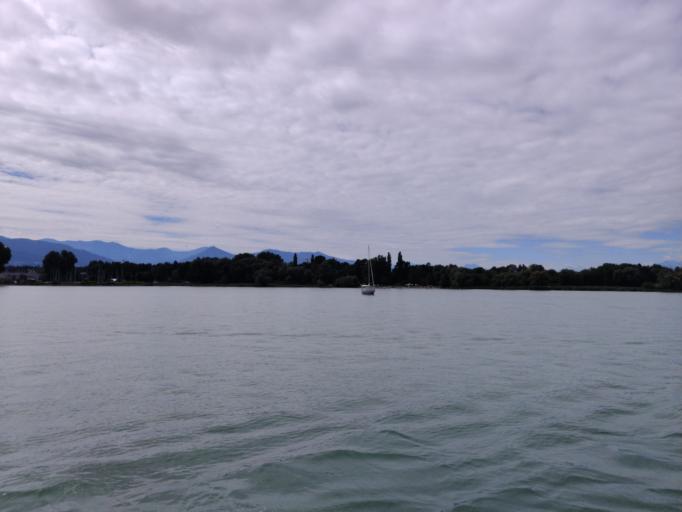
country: AT
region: Vorarlberg
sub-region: Politischer Bezirk Bregenz
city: Lauterach
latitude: 47.5106
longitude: 9.7142
